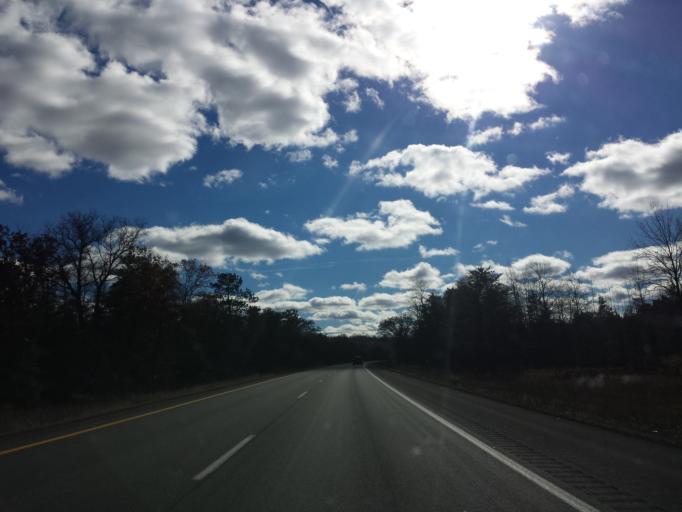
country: US
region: Michigan
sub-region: Cheboygan County
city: Indian River
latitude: 45.3770
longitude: -84.6072
